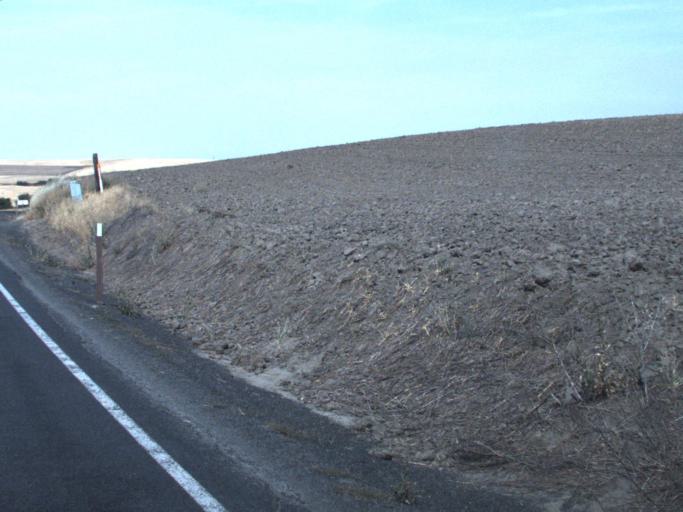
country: US
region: Idaho
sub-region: Benewah County
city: Plummer
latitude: 47.2419
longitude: -117.1302
